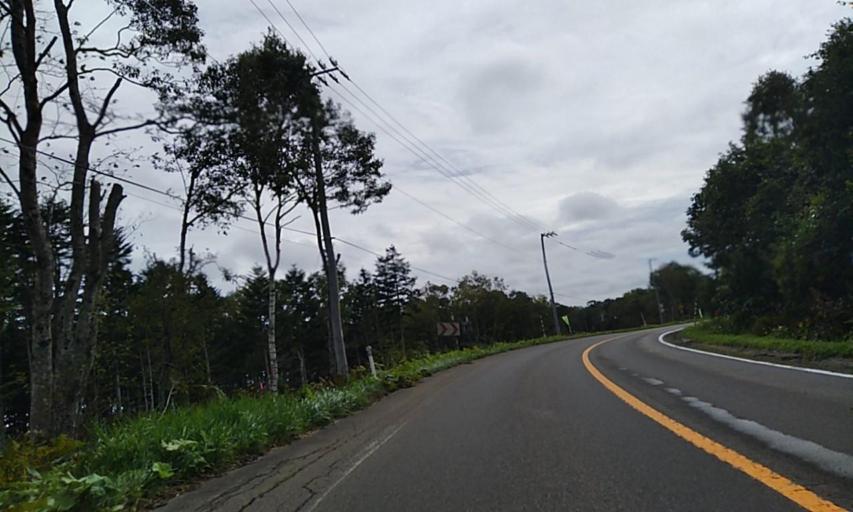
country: JP
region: Hokkaido
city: Shibetsu
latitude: 43.6011
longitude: 145.1927
